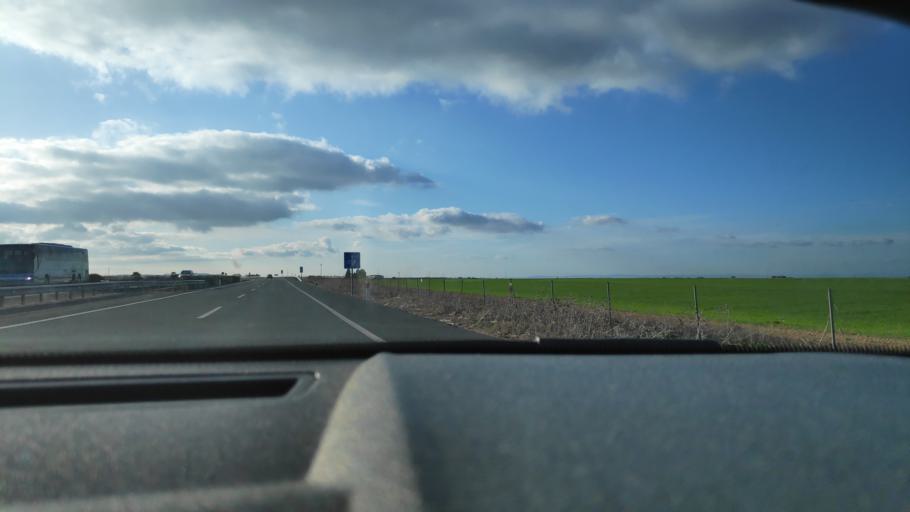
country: ES
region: Andalusia
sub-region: Provincia de Sevilla
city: La Campana
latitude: 37.4897
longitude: -5.5036
